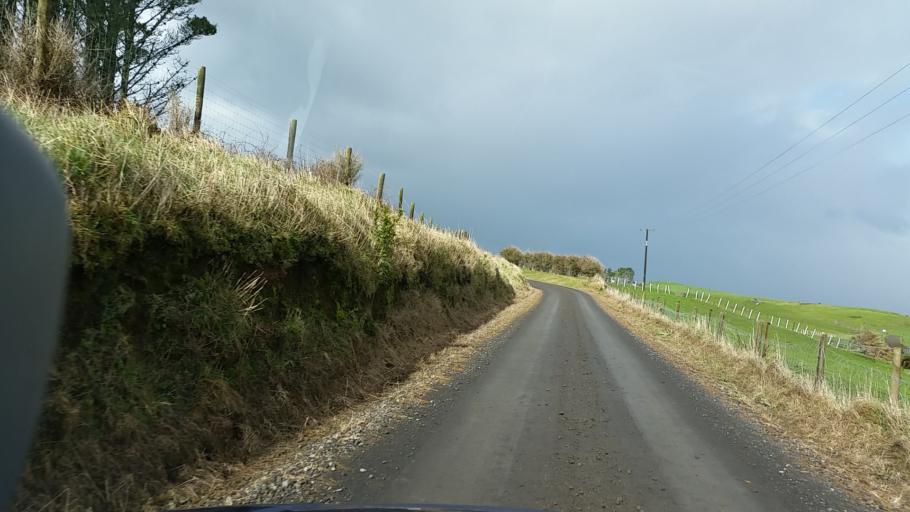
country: NZ
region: Taranaki
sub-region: South Taranaki District
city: Eltham
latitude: -39.2822
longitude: 174.3081
